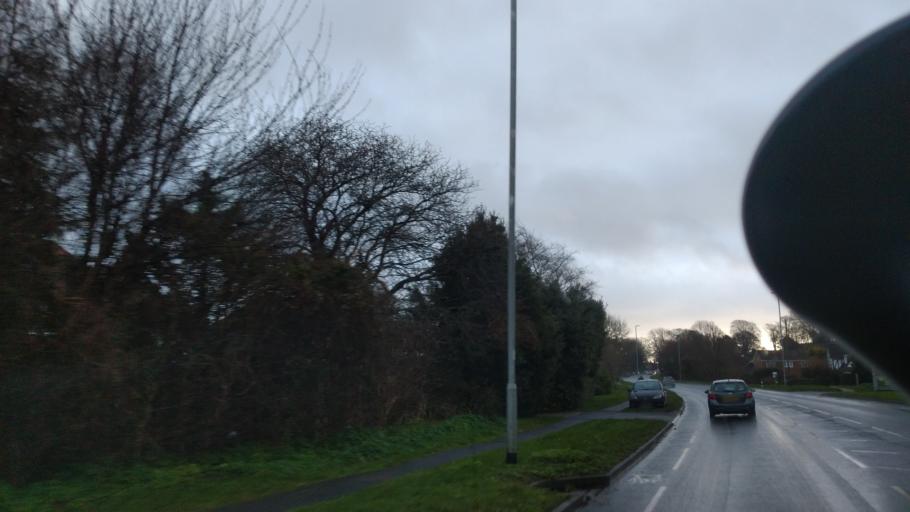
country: GB
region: England
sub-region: East Sussex
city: Eastbourne
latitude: 50.8030
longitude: 0.2508
